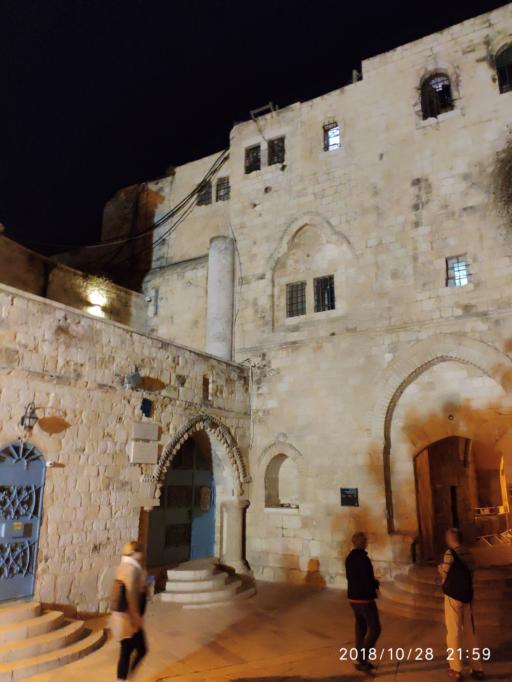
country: PS
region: West Bank
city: Old City
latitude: 31.7719
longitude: 35.2292
